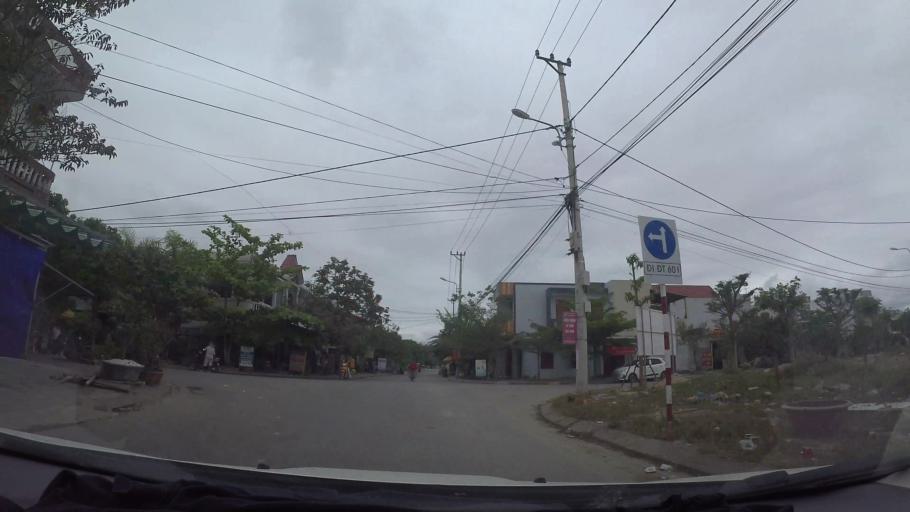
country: VN
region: Da Nang
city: Lien Chieu
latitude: 16.0948
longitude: 108.1032
